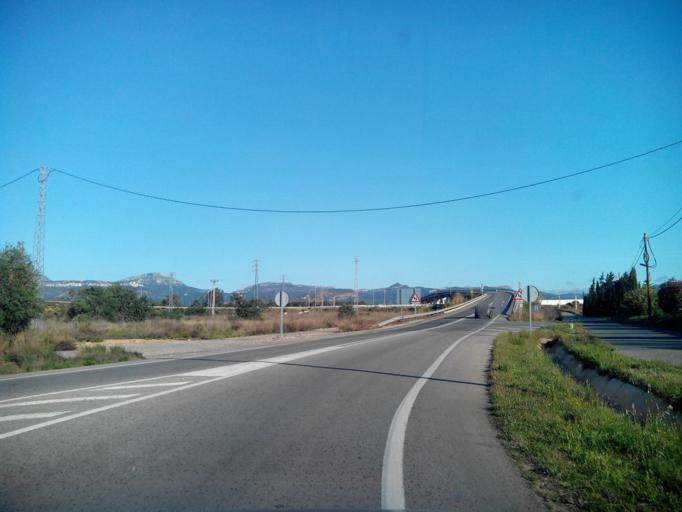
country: ES
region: Catalonia
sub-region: Provincia de Tarragona
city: Cambrils
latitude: 41.0572
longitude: 0.9946
